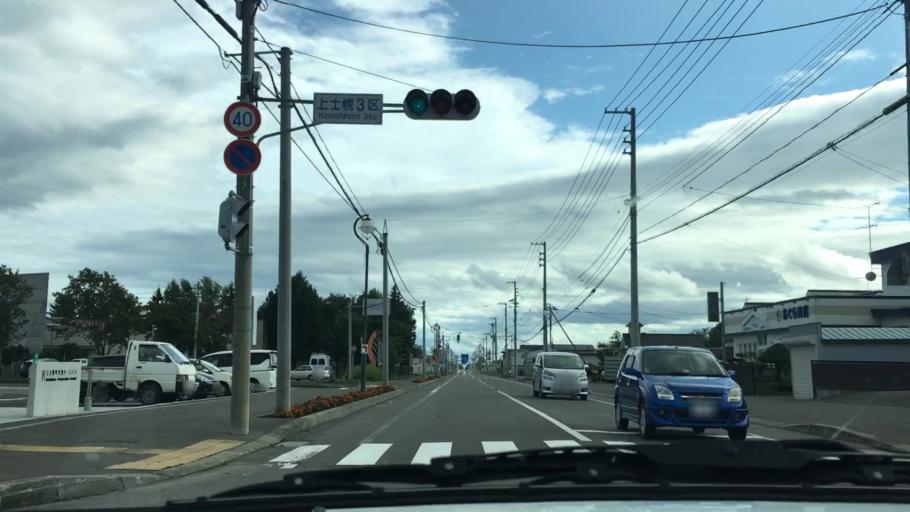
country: JP
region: Hokkaido
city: Otofuke
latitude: 43.2319
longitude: 143.2949
